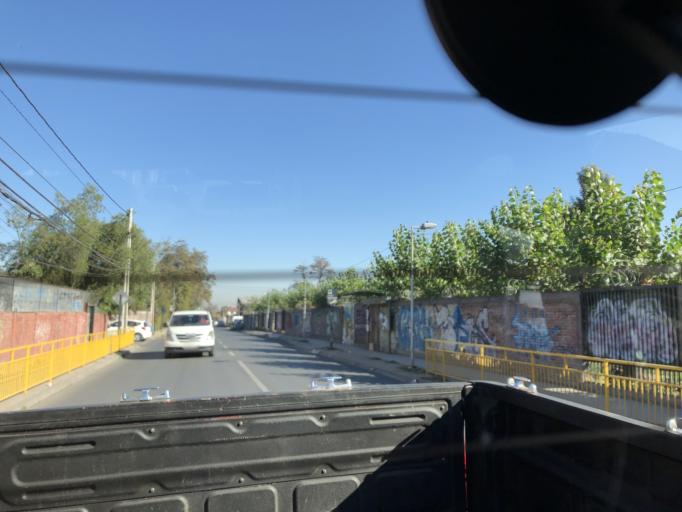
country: CL
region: Santiago Metropolitan
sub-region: Provincia de Cordillera
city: Puente Alto
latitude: -33.5826
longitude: -70.5738
